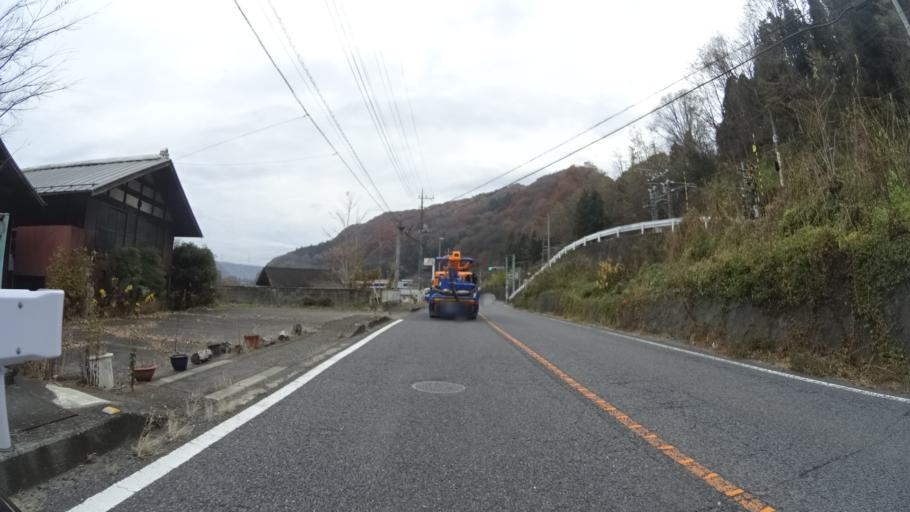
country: JP
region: Gunma
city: Numata
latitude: 36.6130
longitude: 139.0417
